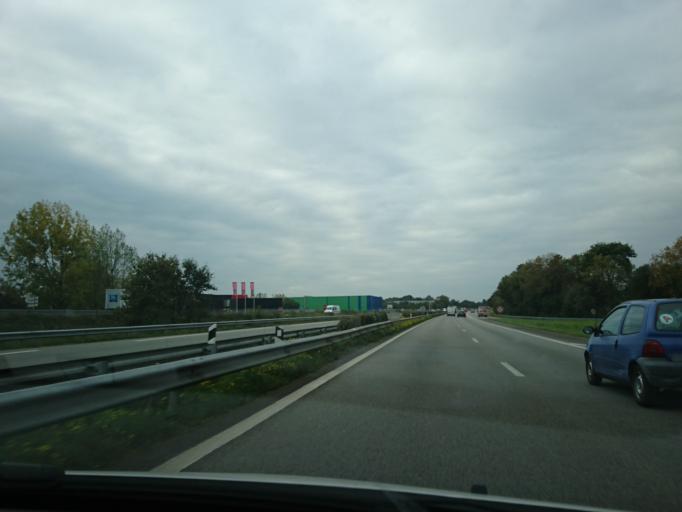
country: FR
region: Pays de la Loire
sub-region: Departement de la Loire-Atlantique
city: Sautron
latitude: 47.2432
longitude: -1.6704
